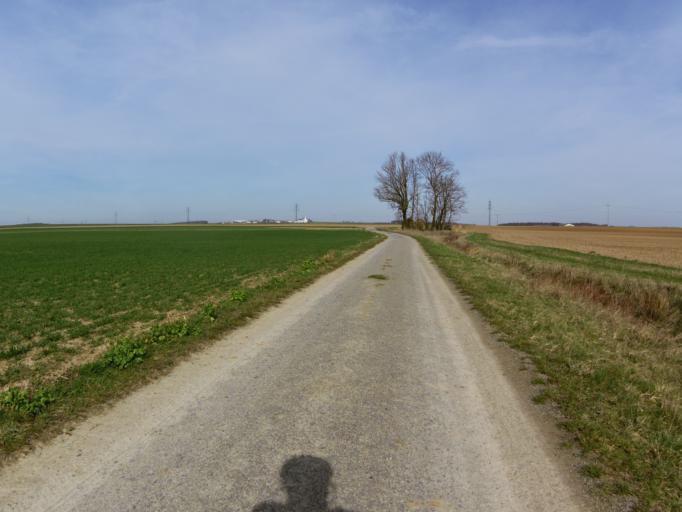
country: DE
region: Bavaria
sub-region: Regierungsbezirk Unterfranken
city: Biebelried
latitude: 49.7499
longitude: 10.0769
